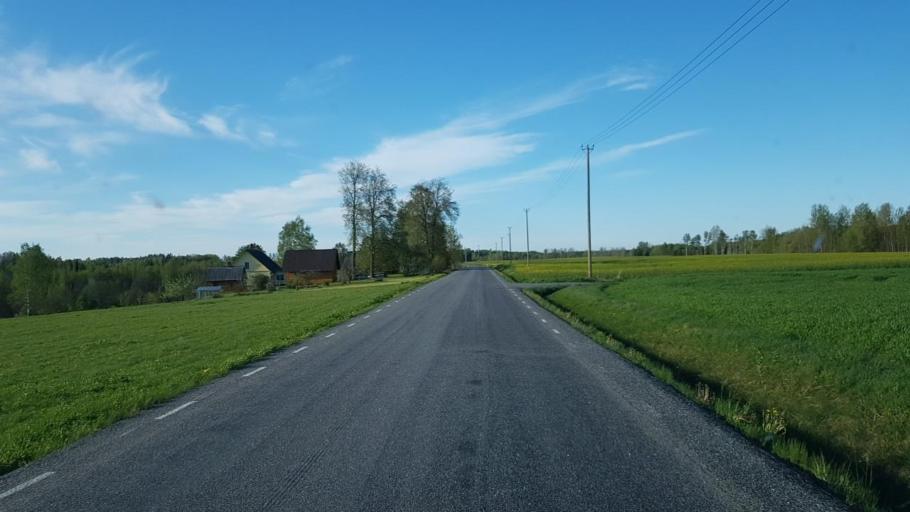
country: EE
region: Polvamaa
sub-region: Polva linn
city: Polva
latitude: 58.0963
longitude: 27.2215
